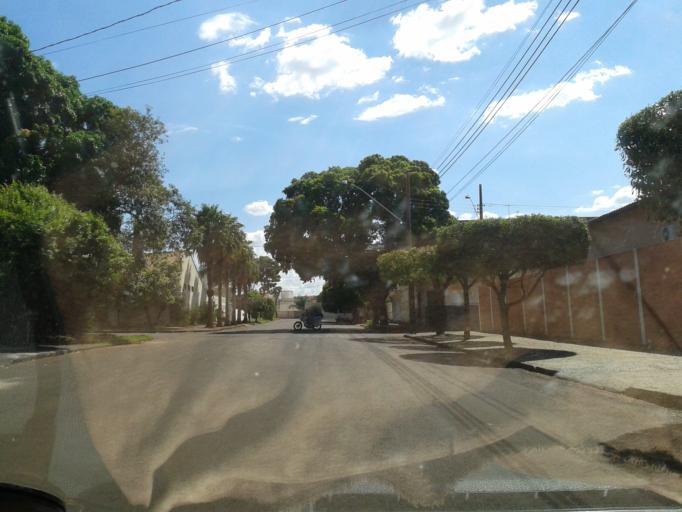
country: BR
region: Minas Gerais
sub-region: Ituiutaba
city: Ituiutaba
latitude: -18.9871
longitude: -49.4566
